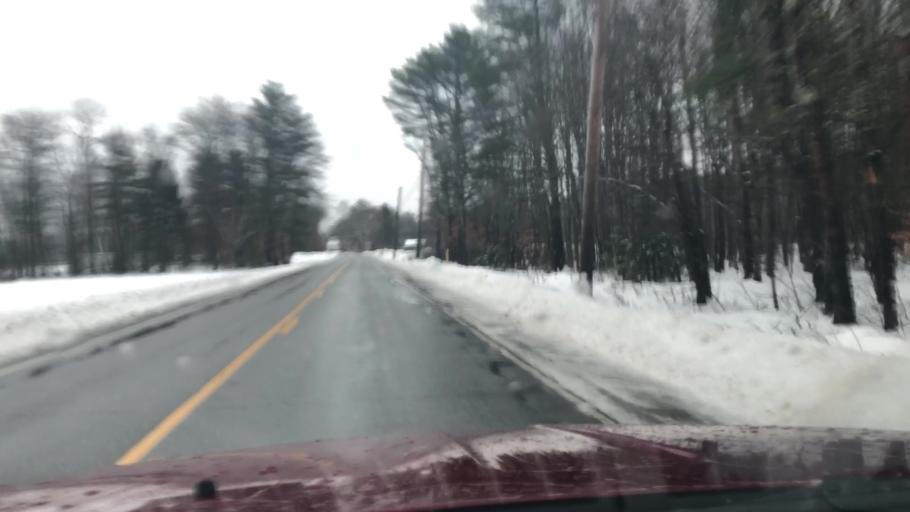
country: US
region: Maine
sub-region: Oxford County
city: Rumford
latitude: 44.4870
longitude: -70.6623
